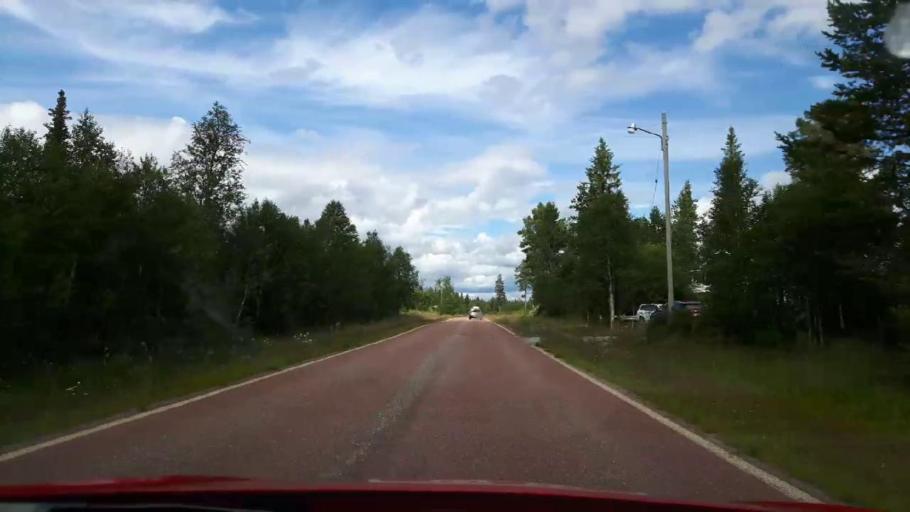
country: NO
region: Hedmark
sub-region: Trysil
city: Innbygda
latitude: 62.0028
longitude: 12.9769
